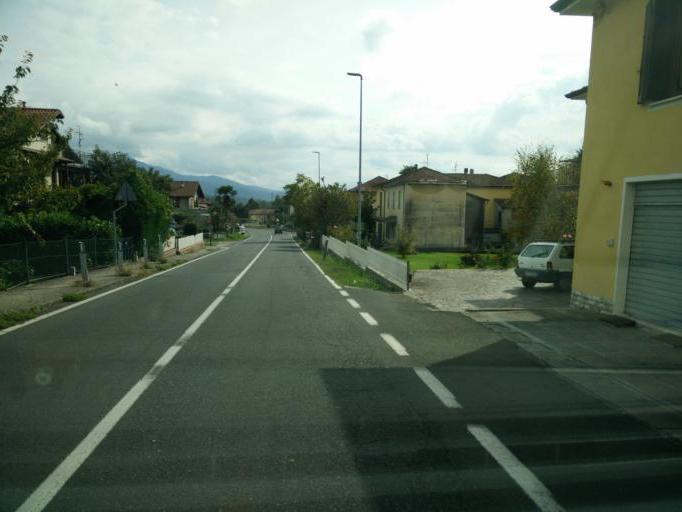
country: IT
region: Tuscany
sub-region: Provincia di Massa-Carrara
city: Filattiera
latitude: 44.3379
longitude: 9.9149
